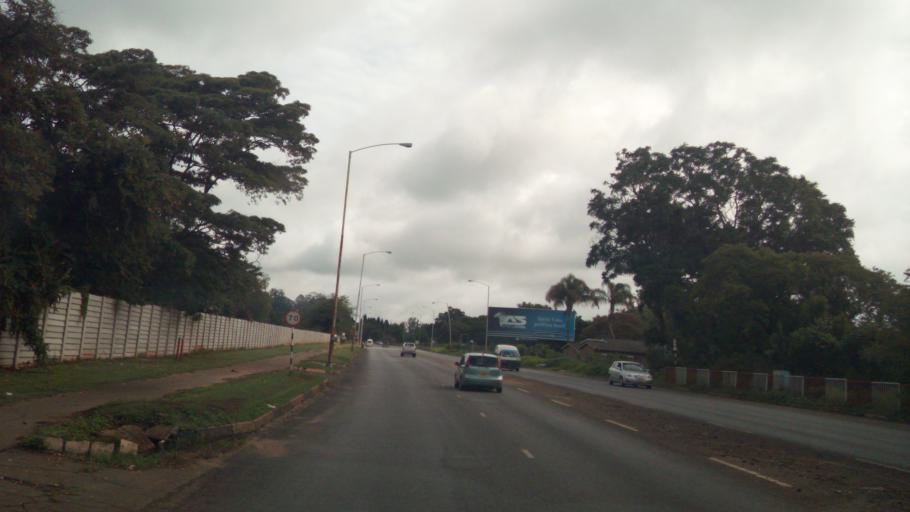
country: ZW
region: Harare
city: Harare
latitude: -17.8047
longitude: 31.0603
